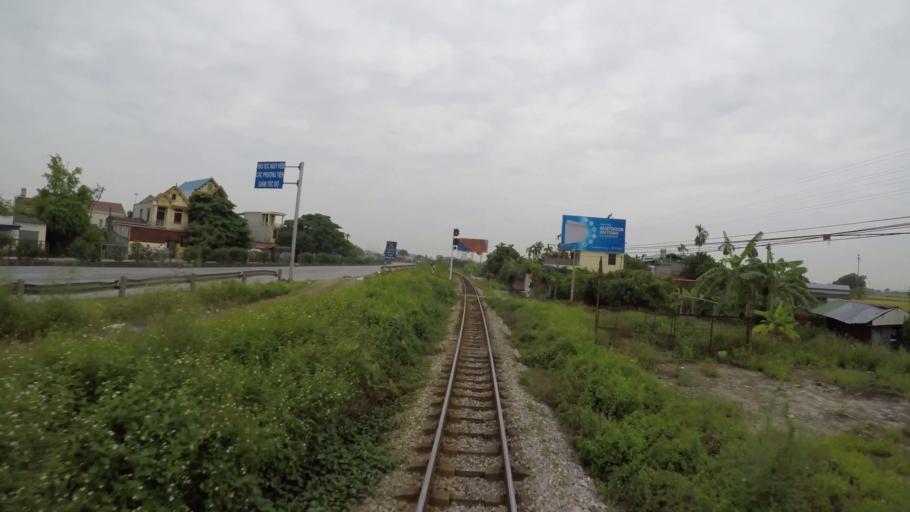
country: VN
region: Hai Duong
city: Phu Thai
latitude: 20.9350
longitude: 106.5504
